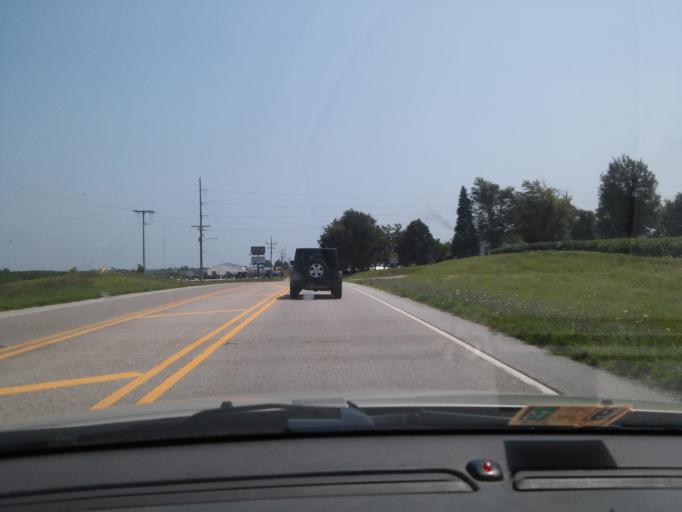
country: US
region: Illinois
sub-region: Pike County
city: Pittsfield
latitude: 39.6047
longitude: -90.8483
